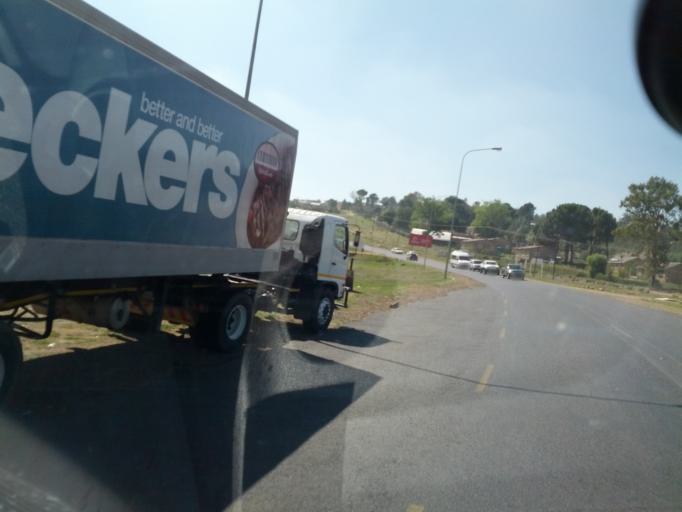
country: LS
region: Berea
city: Teyateyaneng
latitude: -29.1467
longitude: 27.7216
